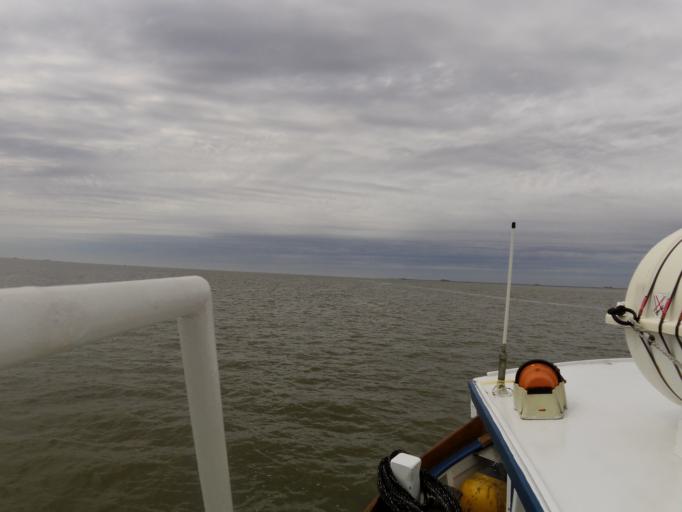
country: DE
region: Schleswig-Holstein
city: Langeness
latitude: 54.6131
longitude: 8.6114
